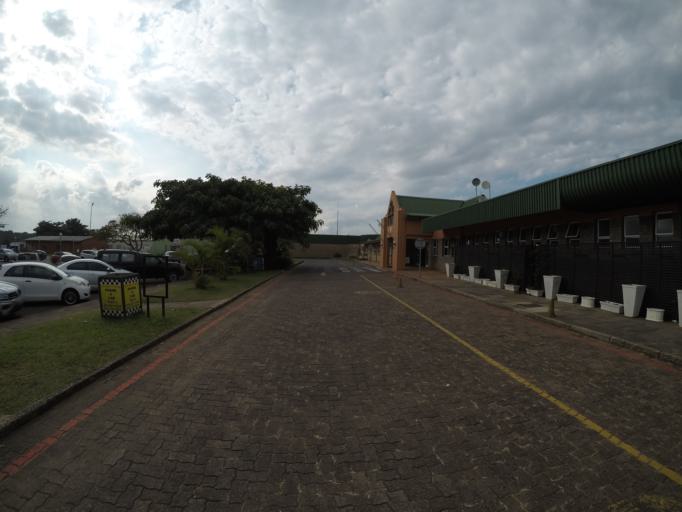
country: ZA
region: KwaZulu-Natal
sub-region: uThungulu District Municipality
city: Richards Bay
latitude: -28.7370
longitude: 32.0936
